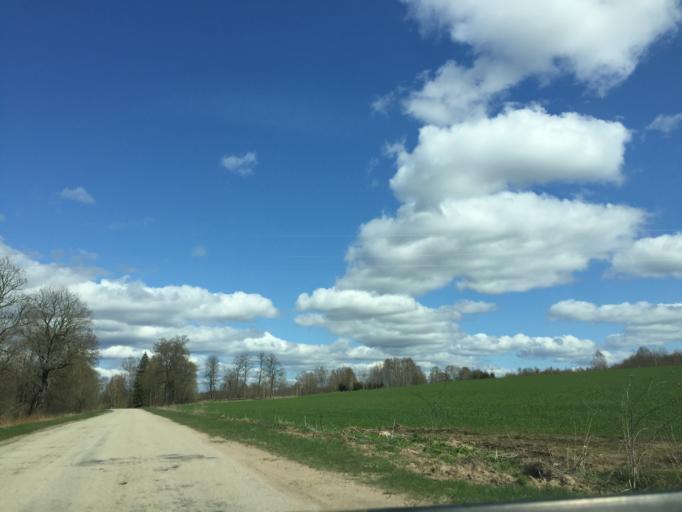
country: LV
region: Rezekne
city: Rezekne
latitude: 56.6821
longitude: 27.2120
